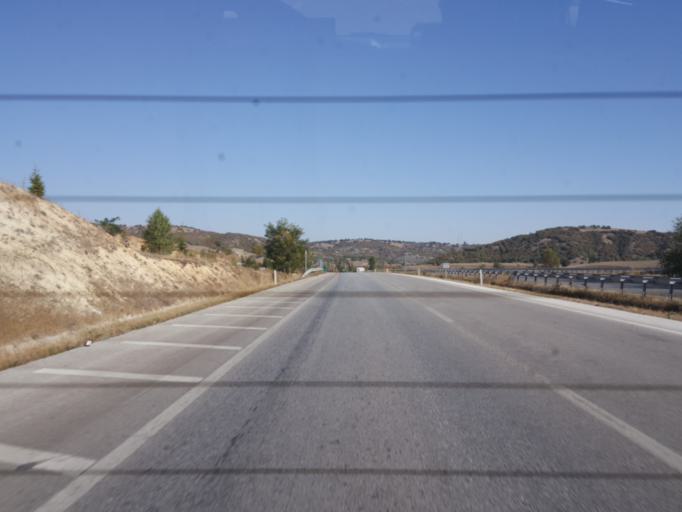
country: TR
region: Corum
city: Alaca
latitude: 40.2946
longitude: 34.6529
